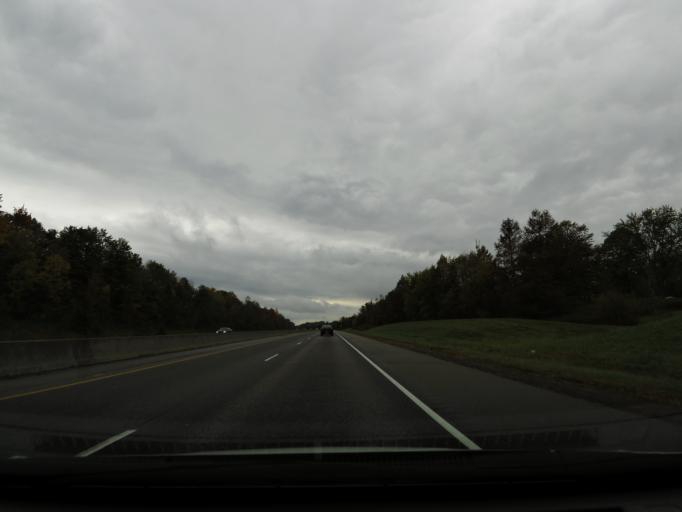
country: CA
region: Ontario
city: Brockville
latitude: 44.6441
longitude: -75.6386
